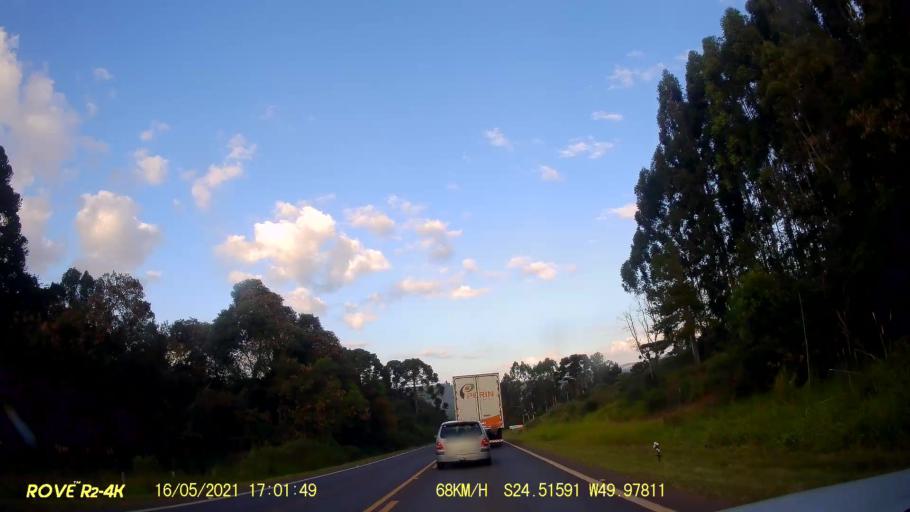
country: BR
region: Parana
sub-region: Pirai Do Sul
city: Pirai do Sul
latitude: -24.5159
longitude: -49.9780
